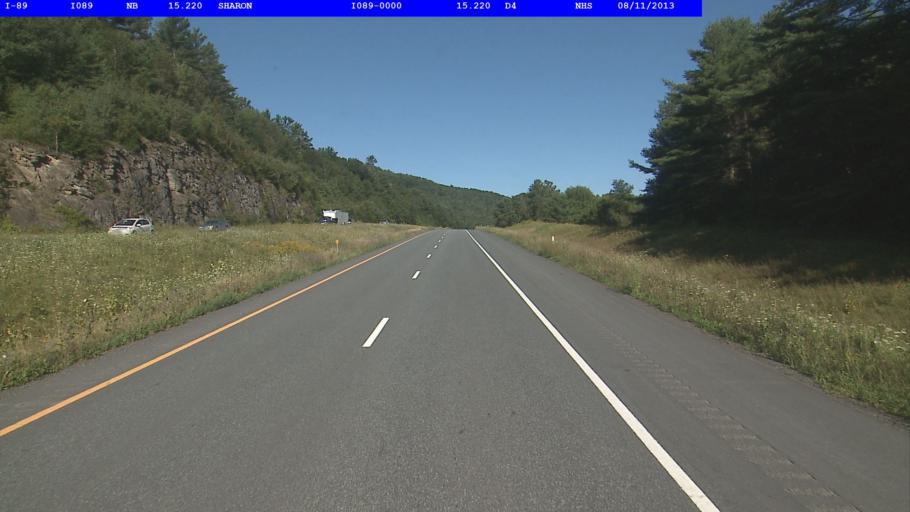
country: US
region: Vermont
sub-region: Windsor County
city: Woodstock
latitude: 43.7841
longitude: -72.4869
